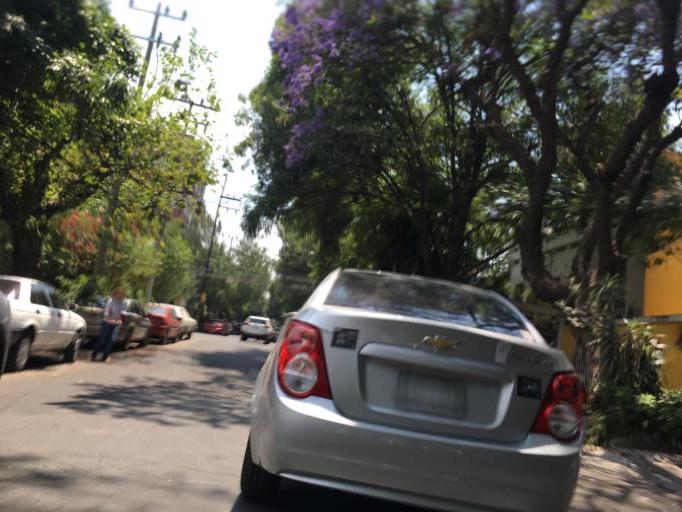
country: MX
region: Mexico City
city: Benito Juarez
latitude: 19.4164
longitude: -99.1741
